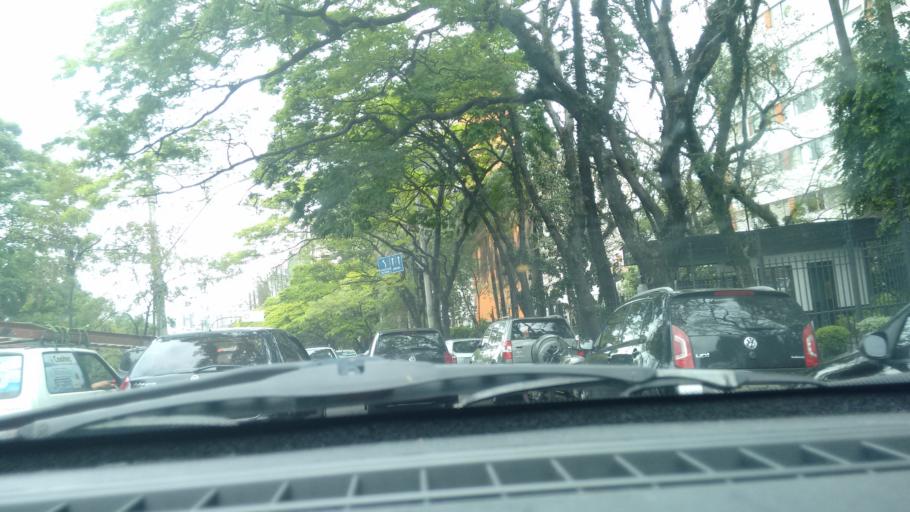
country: BR
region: Rio Grande do Sul
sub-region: Porto Alegre
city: Porto Alegre
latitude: -30.0304
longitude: -51.1831
